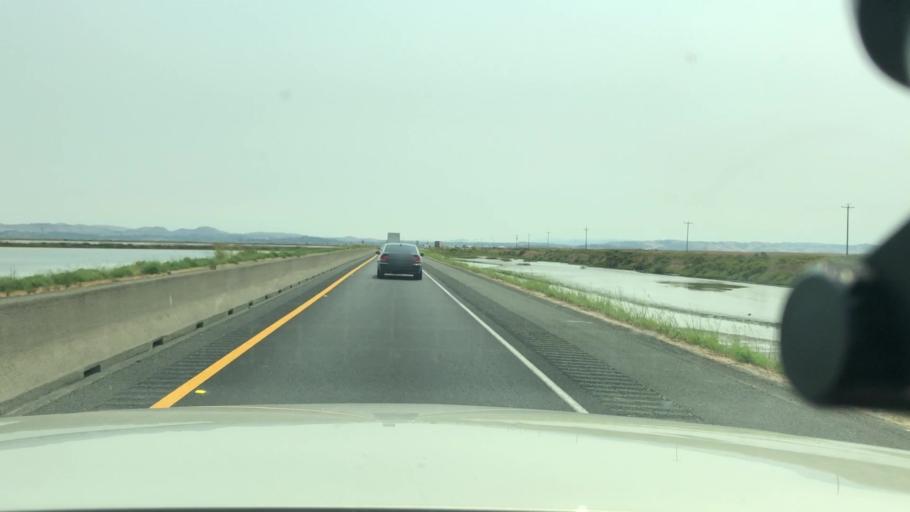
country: US
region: California
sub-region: Napa County
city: American Canyon
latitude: 38.1398
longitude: -122.3578
